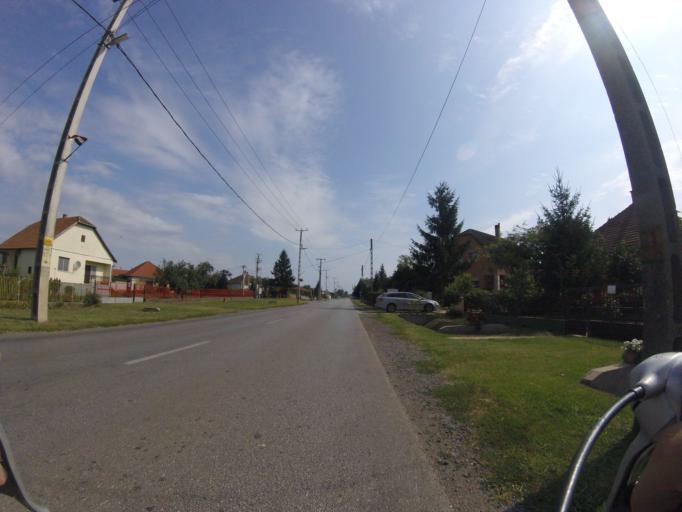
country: HU
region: Szabolcs-Szatmar-Bereg
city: Kemecse
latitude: 48.0642
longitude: 21.7932
